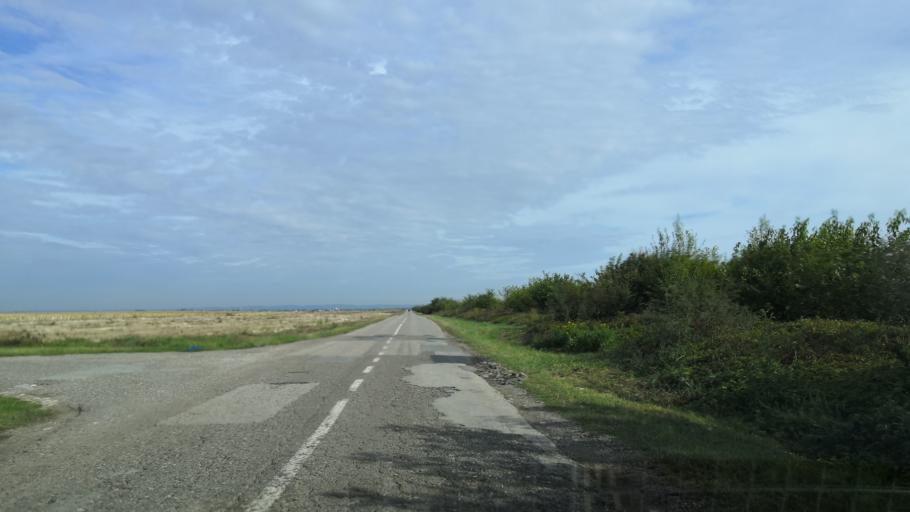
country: RS
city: Novi Karlovci
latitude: 45.0315
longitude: 20.1724
